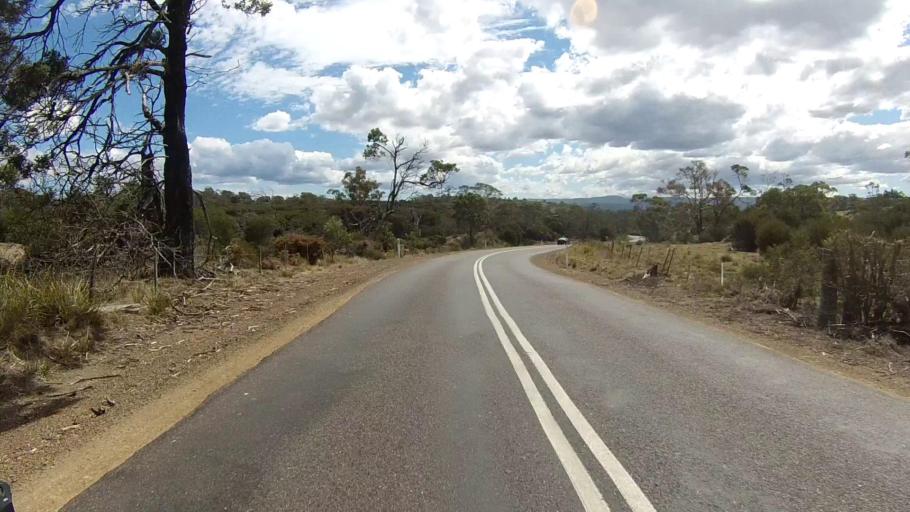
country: AU
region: Tasmania
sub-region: Break O'Day
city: St Helens
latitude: -41.9932
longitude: 148.1128
